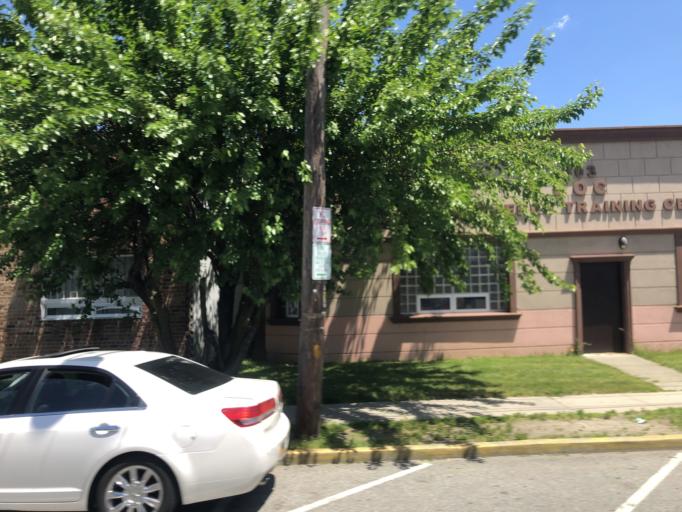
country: US
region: New York
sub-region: Nassau County
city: Roosevelt
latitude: 40.6728
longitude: -73.5812
